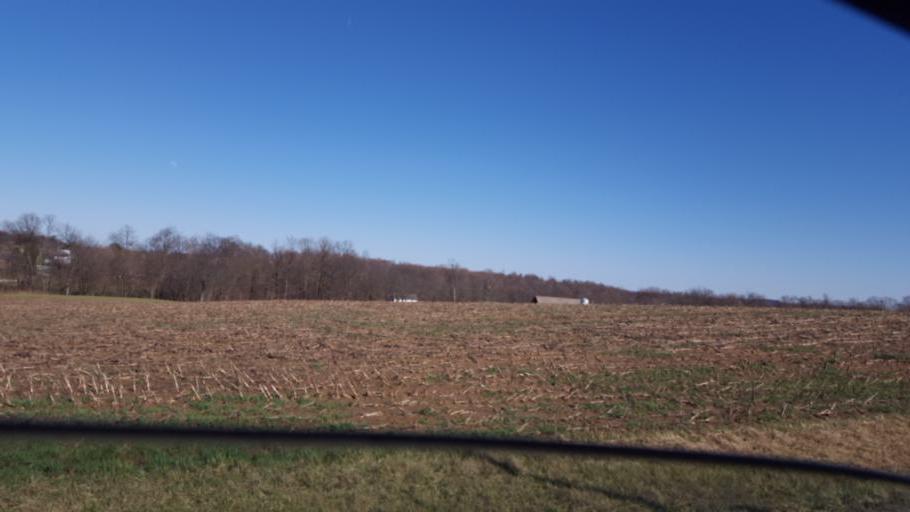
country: US
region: Ohio
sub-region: Wayne County
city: Dalton
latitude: 40.7319
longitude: -81.6969
